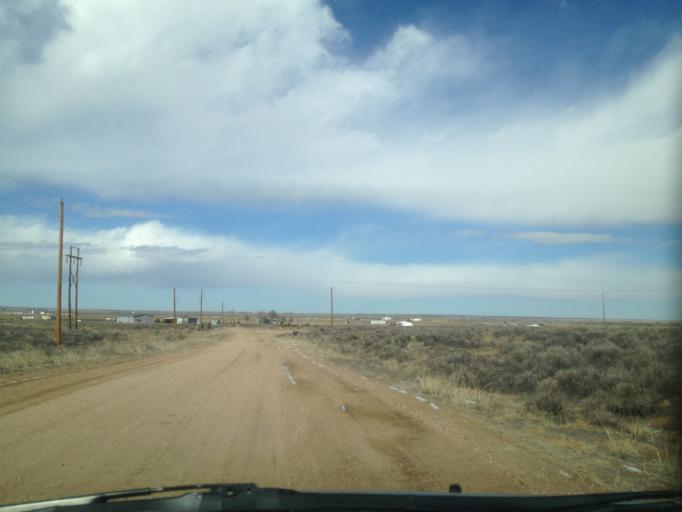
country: US
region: Colorado
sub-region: Weld County
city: Keenesburg
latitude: 40.2826
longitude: -104.2590
